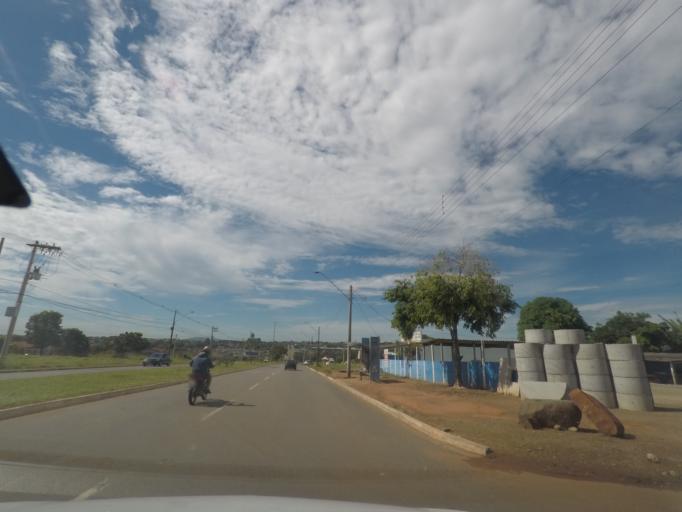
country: BR
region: Goias
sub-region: Aparecida De Goiania
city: Aparecida de Goiania
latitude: -16.8098
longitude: -49.2811
